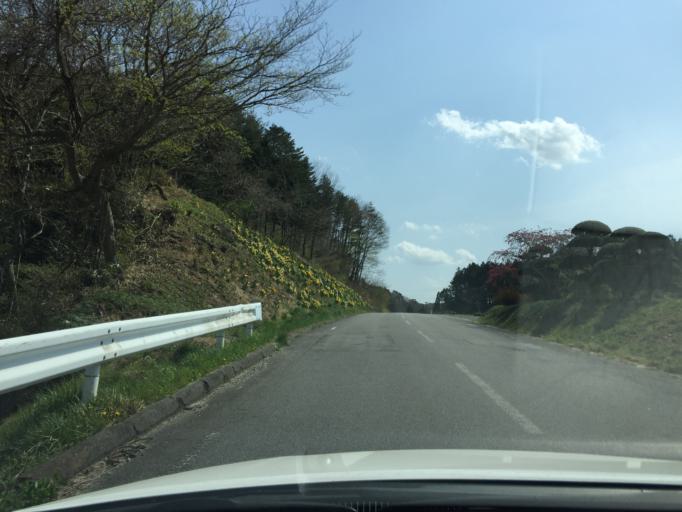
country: JP
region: Fukushima
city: Namie
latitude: 37.3993
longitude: 140.8018
